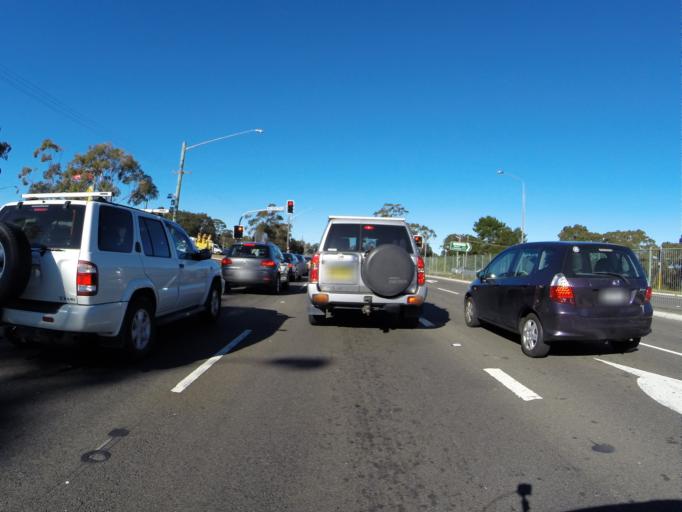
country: AU
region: New South Wales
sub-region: Sutherland Shire
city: Heathcote
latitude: -34.0788
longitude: 151.0107
